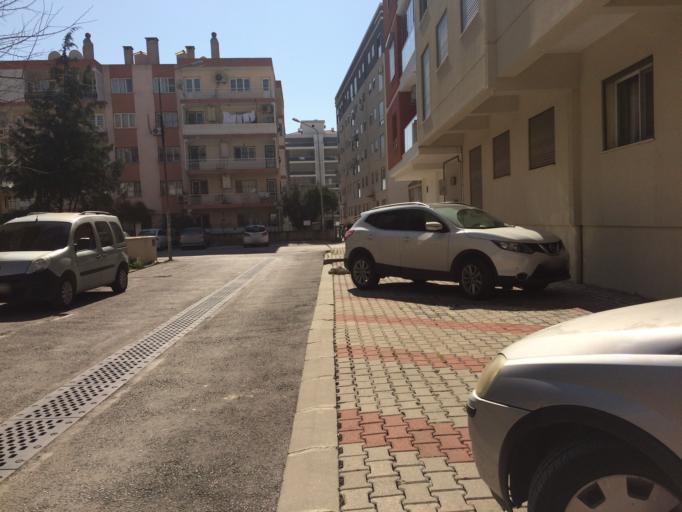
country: TR
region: Izmir
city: Karsiyaka
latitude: 38.4894
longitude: 27.0601
